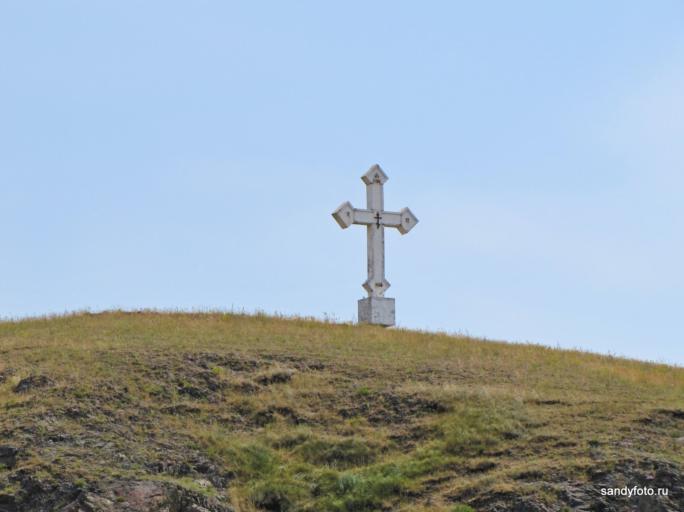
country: RU
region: Chelyabinsk
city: Troitsk
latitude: 54.0805
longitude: 61.5799
